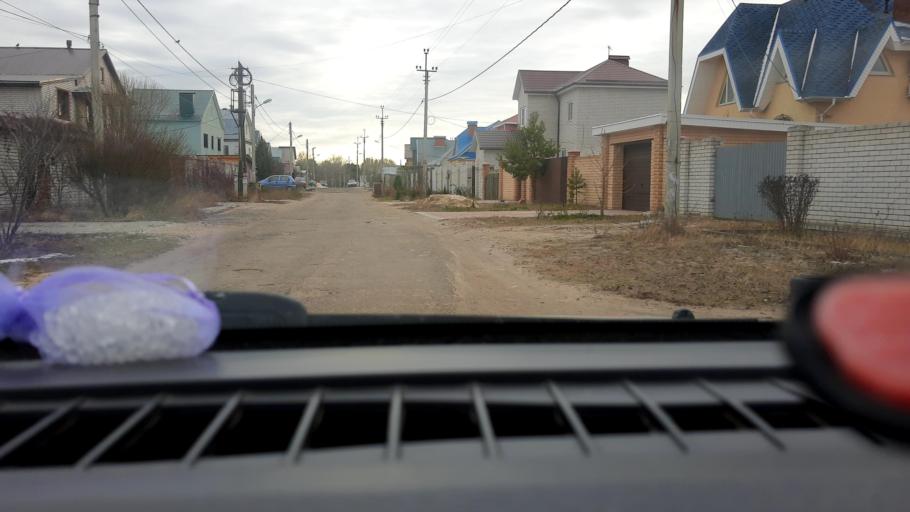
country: RU
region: Nizjnij Novgorod
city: Gorbatovka
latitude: 56.3848
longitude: 43.7723
